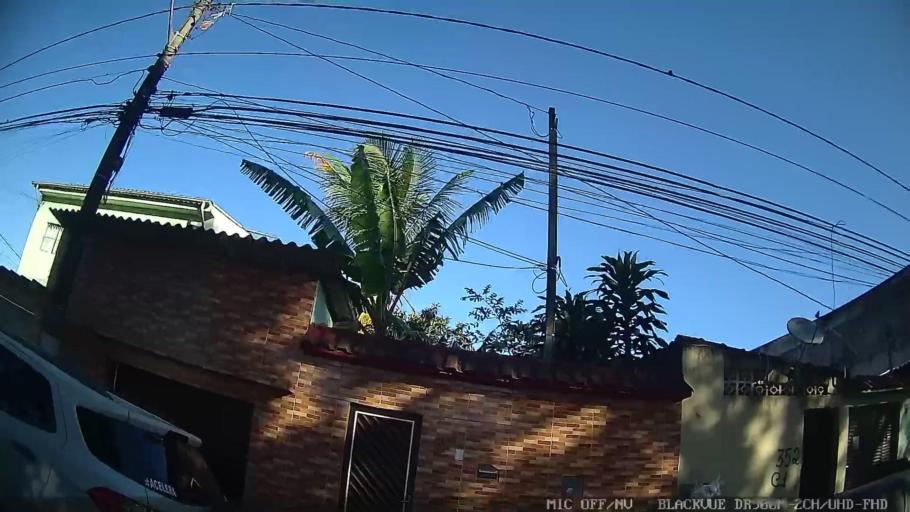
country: BR
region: Sao Paulo
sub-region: Santos
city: Santos
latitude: -23.9456
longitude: -46.2948
